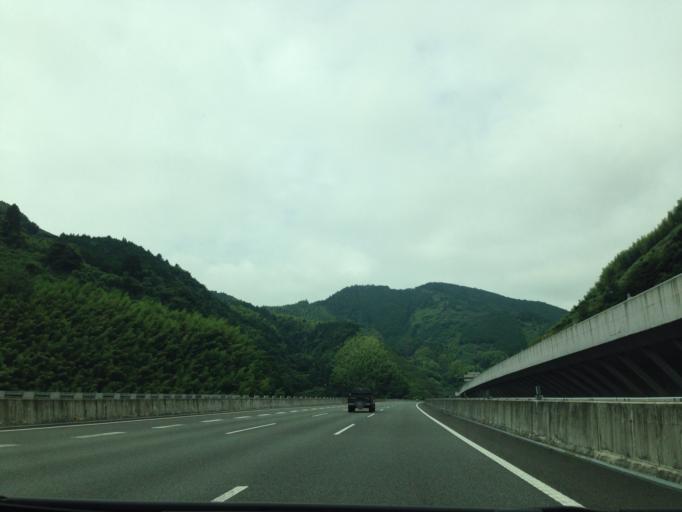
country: JP
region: Shizuoka
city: Shizuoka-shi
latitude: 35.0696
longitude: 138.4553
